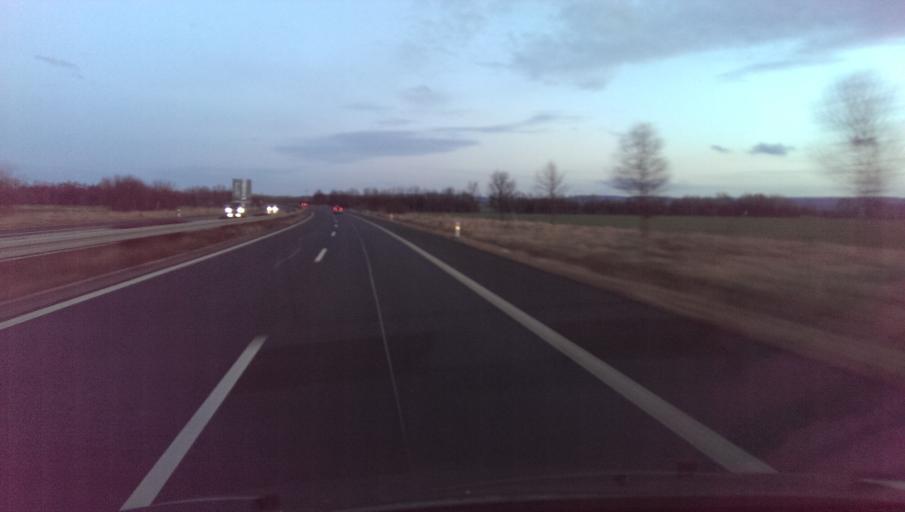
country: DE
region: Saxony-Anhalt
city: Veckenstedt
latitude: 51.8838
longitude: 10.7208
